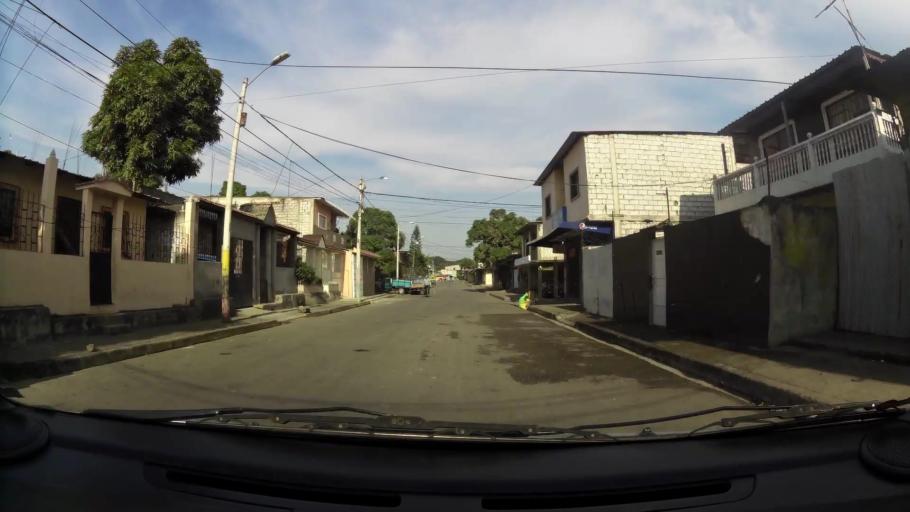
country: EC
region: Guayas
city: Eloy Alfaro
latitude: -2.0733
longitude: -79.9311
